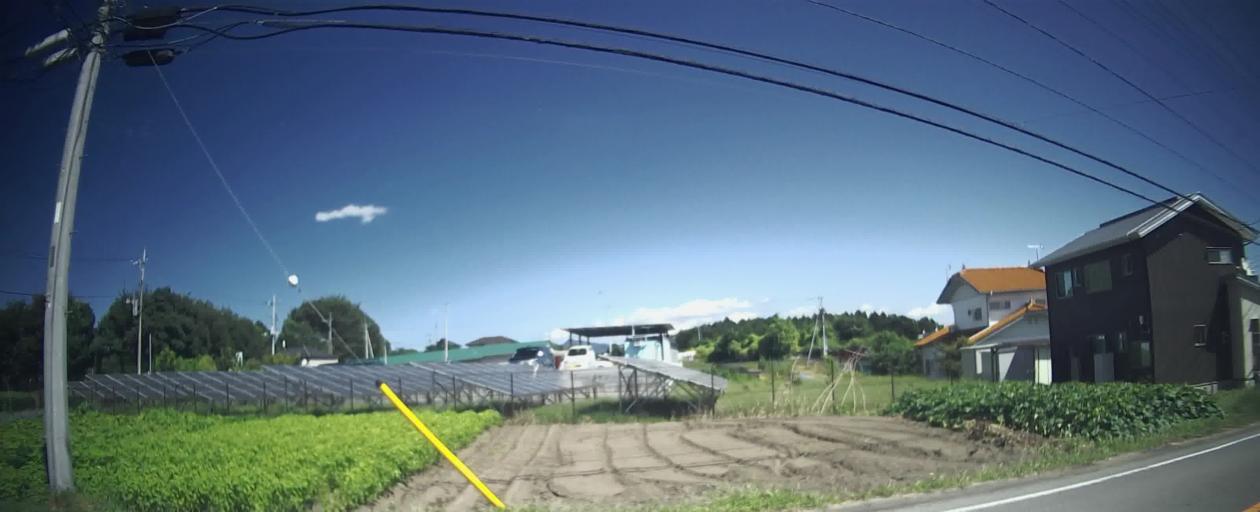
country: JP
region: Gunma
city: Kanekomachi
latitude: 36.4099
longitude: 138.9488
